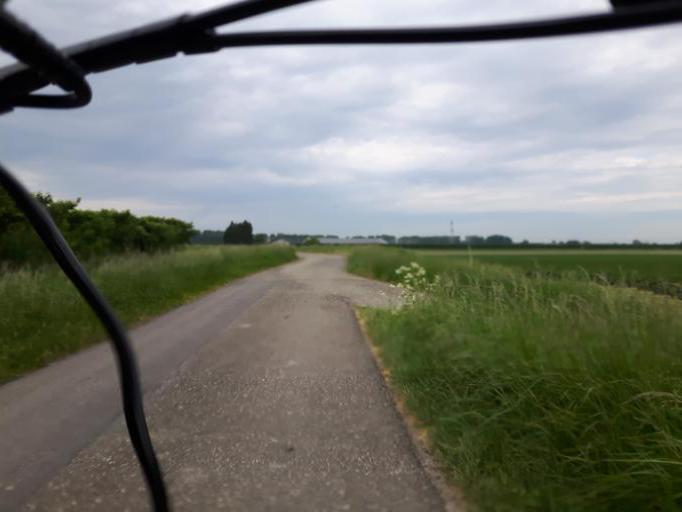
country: NL
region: Zeeland
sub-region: Gemeente Borsele
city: Borssele
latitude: 51.4395
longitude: 3.8191
